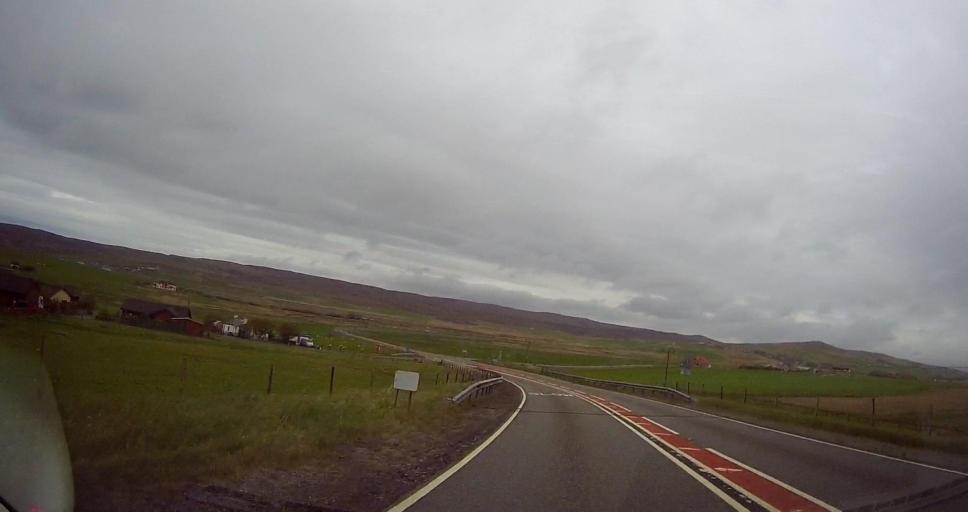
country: GB
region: Scotland
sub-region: Shetland Islands
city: Lerwick
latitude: 60.1846
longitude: -1.2245
